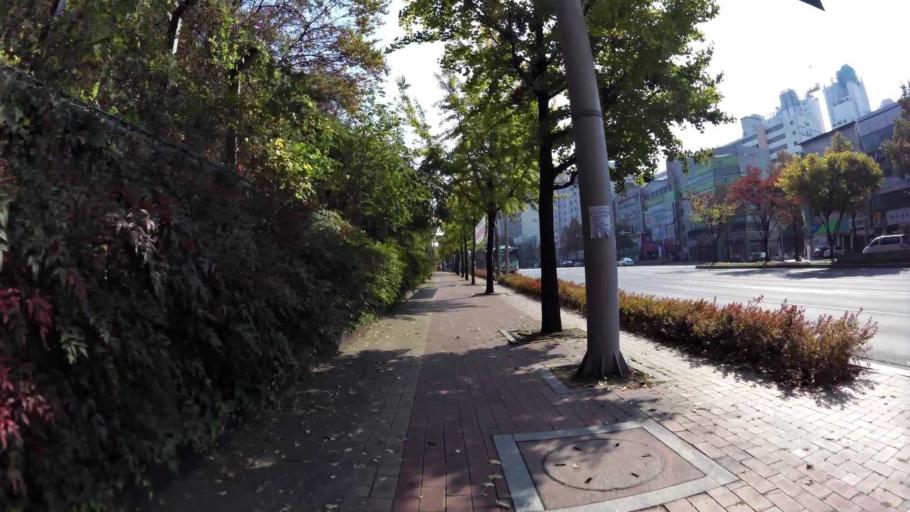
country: KR
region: Daegu
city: Daegu
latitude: 35.8557
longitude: 128.6528
